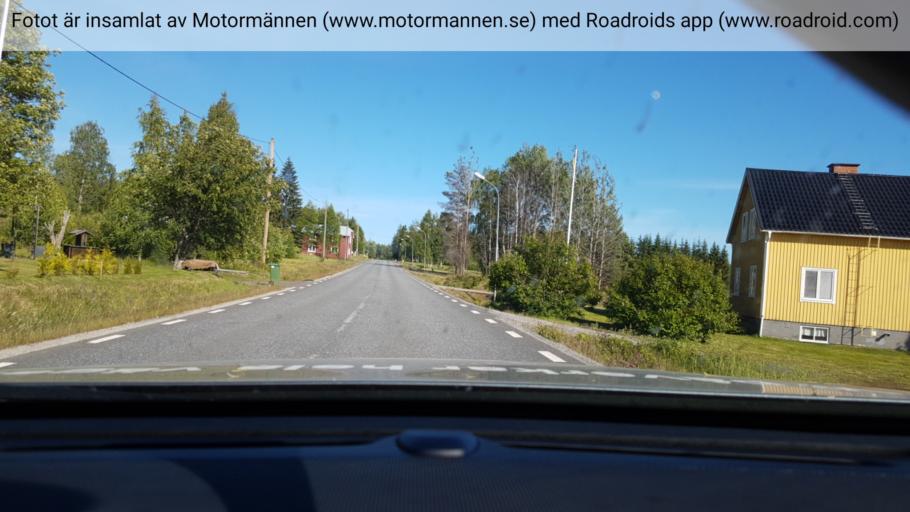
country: SE
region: Vaesterbotten
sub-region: Lycksele Kommun
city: Lycksele
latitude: 64.3986
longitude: 19.0416
